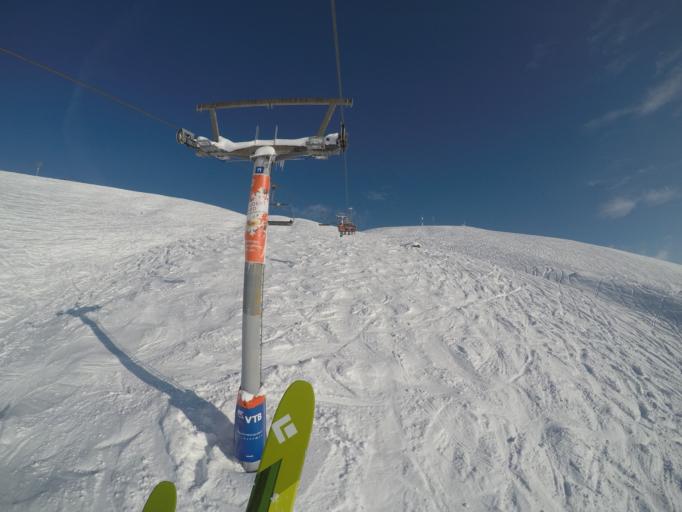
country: GE
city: Gudauri
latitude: 42.4848
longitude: 44.4960
